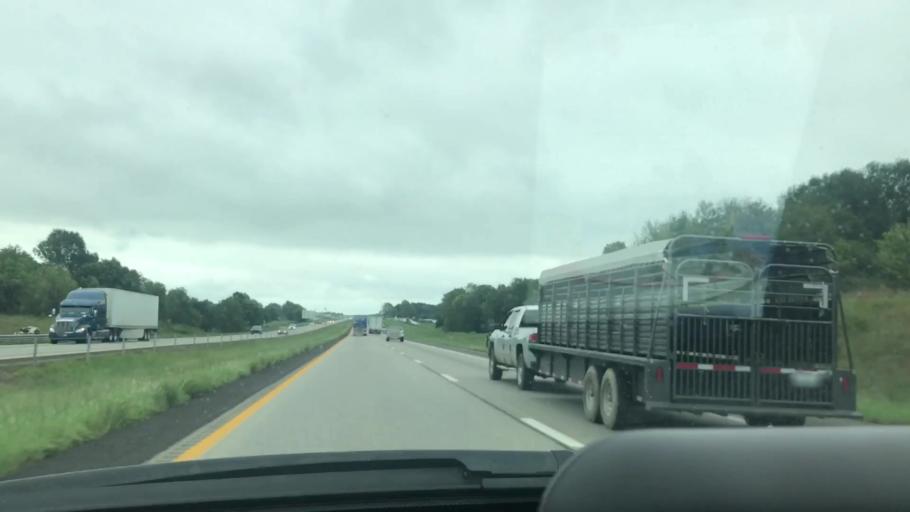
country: US
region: Missouri
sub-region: Greene County
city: Republic
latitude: 37.1962
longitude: -93.4433
